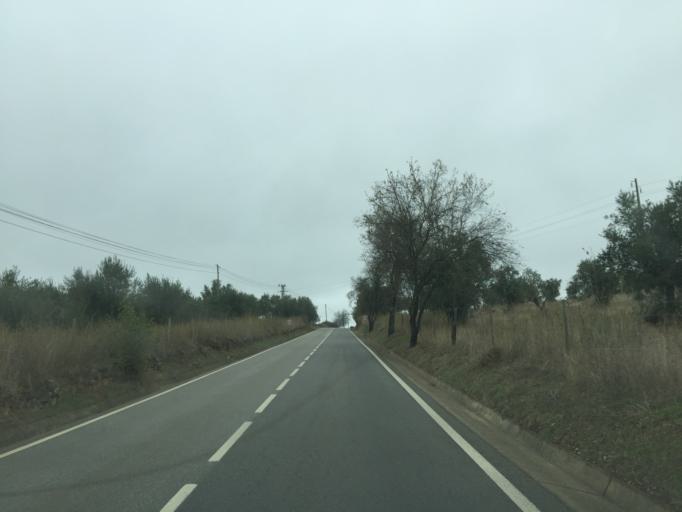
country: PT
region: Portalegre
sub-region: Alter do Chao
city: Alter do Chao
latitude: 39.2096
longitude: -7.6564
